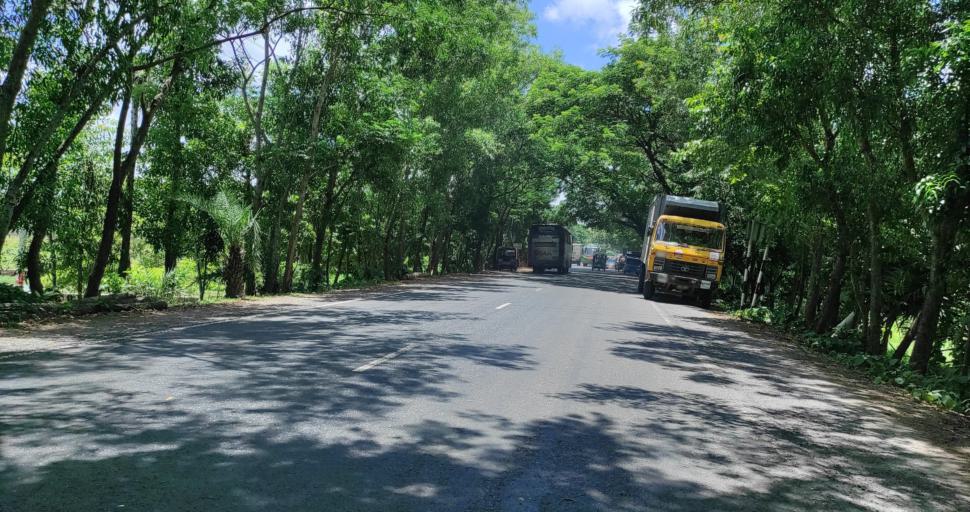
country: BD
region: Barisal
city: Gaurnadi
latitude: 22.8325
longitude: 90.2555
